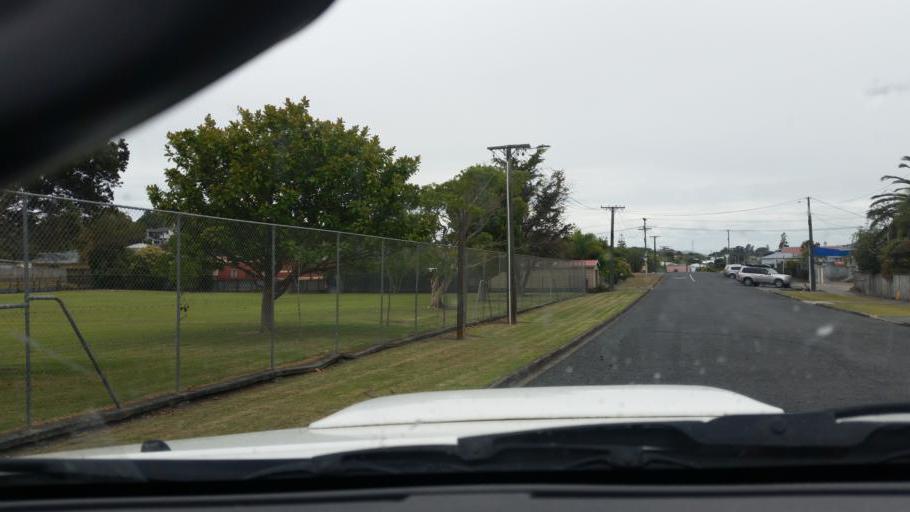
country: NZ
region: Northland
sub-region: Kaipara District
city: Dargaville
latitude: -35.9381
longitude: 173.8667
